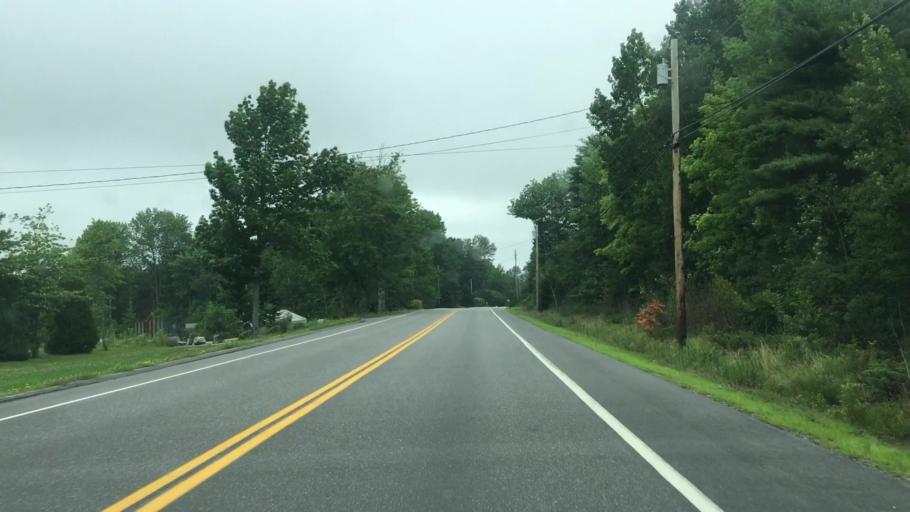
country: US
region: Maine
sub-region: Sagadahoc County
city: Richmond
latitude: 44.0948
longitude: -69.7140
